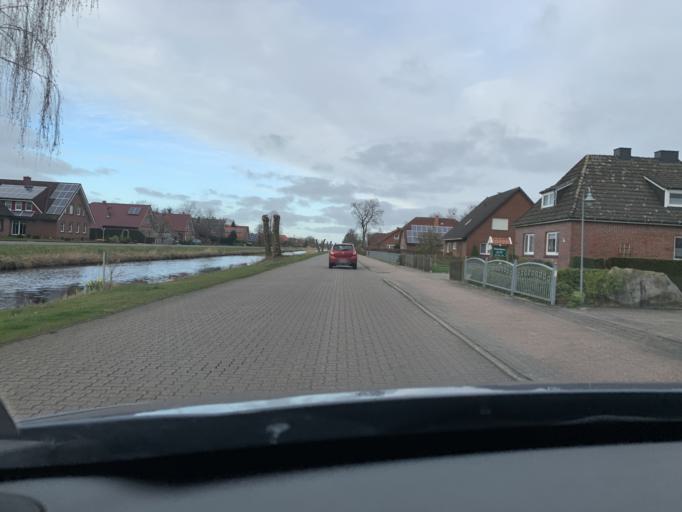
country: DE
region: Lower Saxony
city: Schwerinsdorf
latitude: 53.2718
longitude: 7.6979
